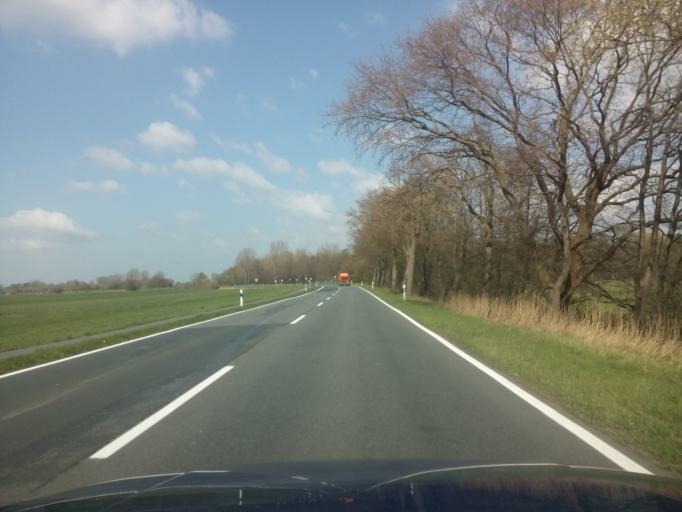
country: DE
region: Lower Saxony
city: Osterholz-Scharmbeck
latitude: 53.1885
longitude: 8.8198
